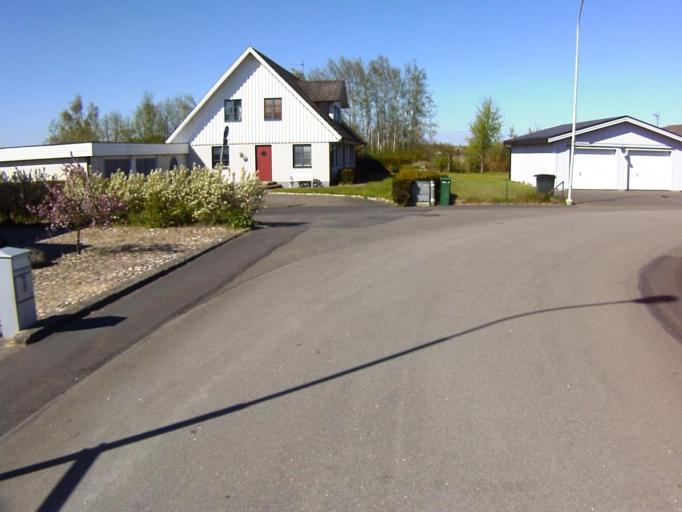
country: SE
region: Skane
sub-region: Kristianstads Kommun
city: Kristianstad
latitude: 56.0344
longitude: 14.1946
